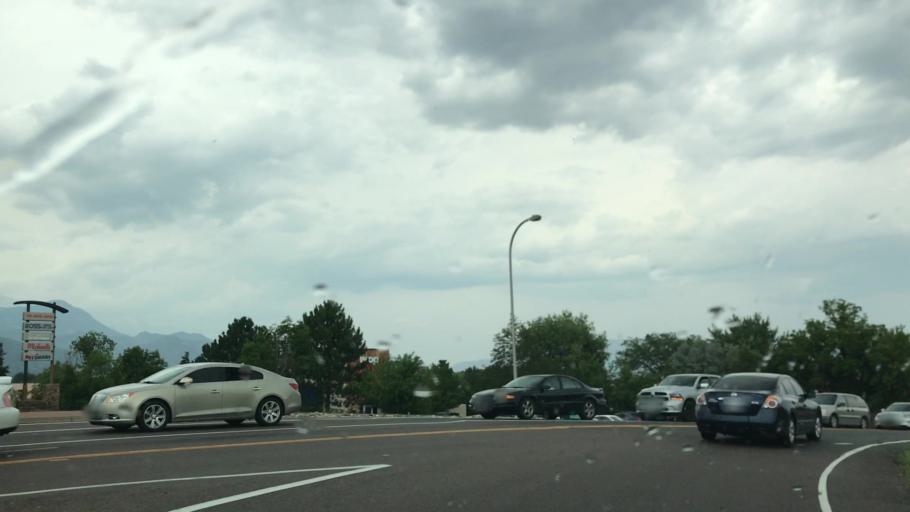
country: US
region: Colorado
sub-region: El Paso County
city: Colorado Springs
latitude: 38.7981
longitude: -104.8173
